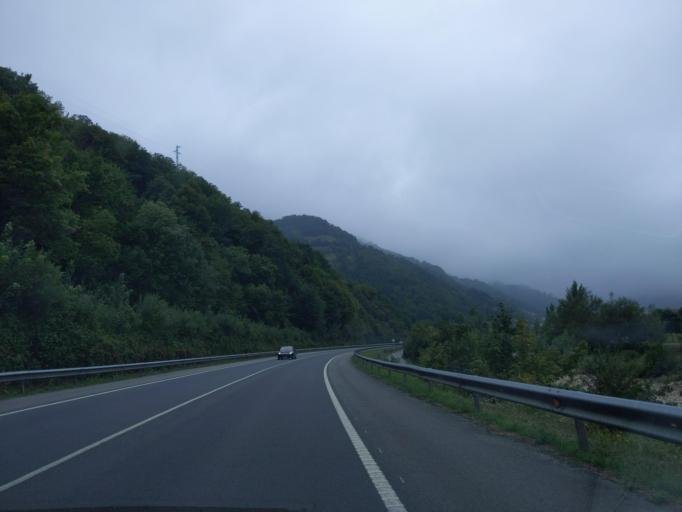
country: ES
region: Asturias
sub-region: Province of Asturias
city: Pola de Laviana
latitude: 43.2363
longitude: -5.5612
